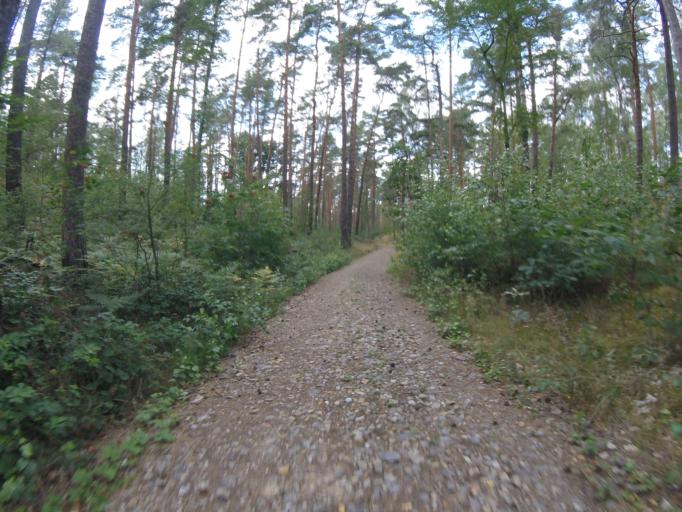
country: DE
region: Brandenburg
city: Schlepzig
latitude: 52.0597
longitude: 13.8014
